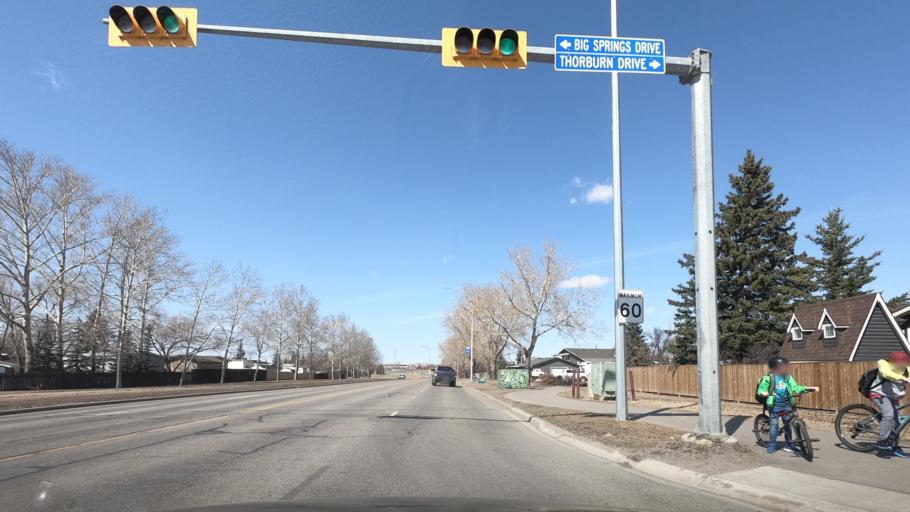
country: CA
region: Alberta
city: Airdrie
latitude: 51.2803
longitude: -113.9898
